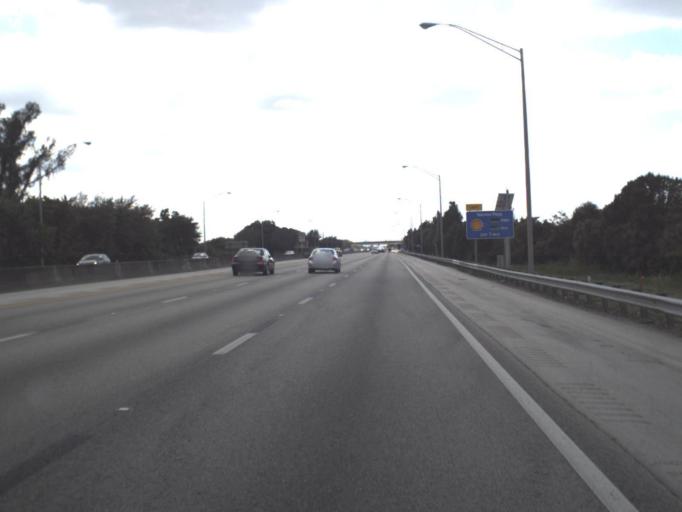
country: US
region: Florida
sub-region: Broward County
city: Coconut Creek
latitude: 26.2381
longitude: -80.1720
